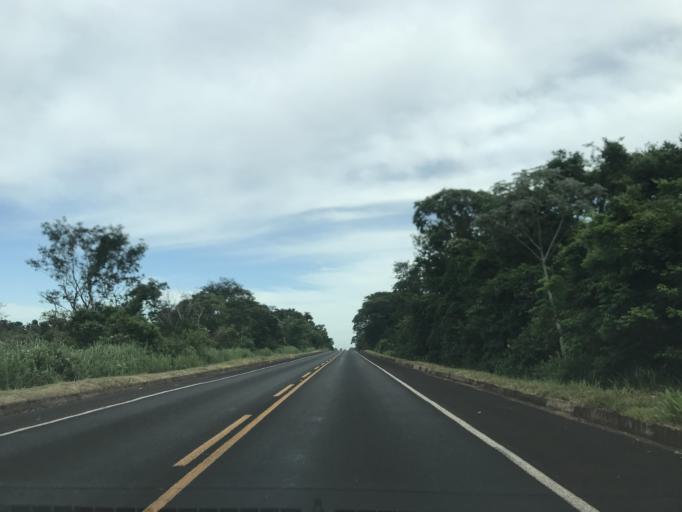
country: BR
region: Parana
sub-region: Paranavai
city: Paranavai
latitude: -23.0211
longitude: -52.4978
